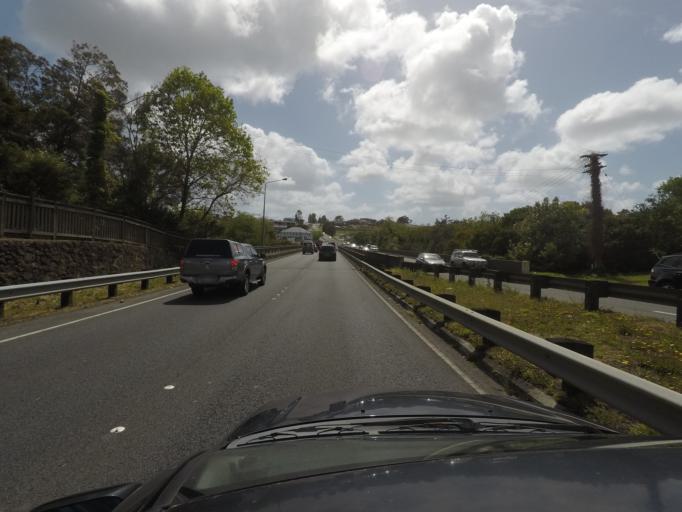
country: NZ
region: Auckland
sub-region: Auckland
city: Rothesay Bay
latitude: -36.6200
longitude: 174.6754
